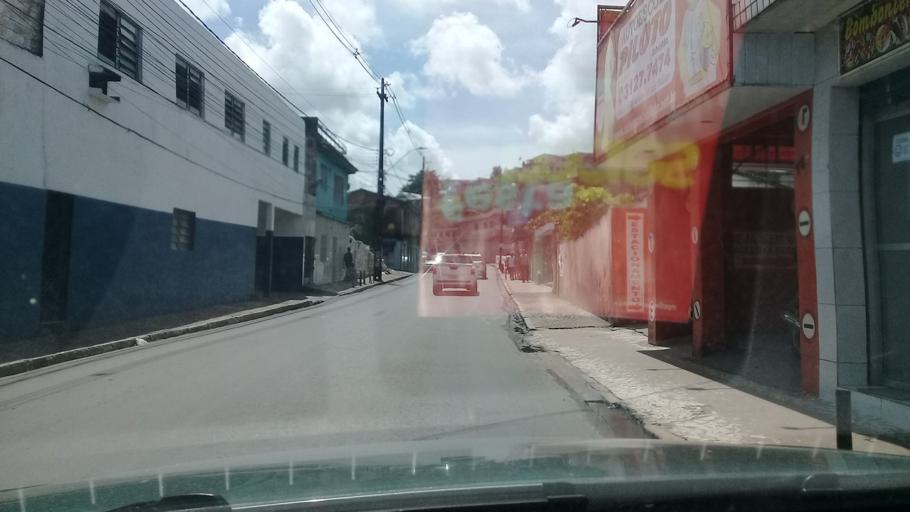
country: BR
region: Pernambuco
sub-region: Jaboatao Dos Guararapes
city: Jaboatao dos Guararapes
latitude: -8.1104
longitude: -35.0162
